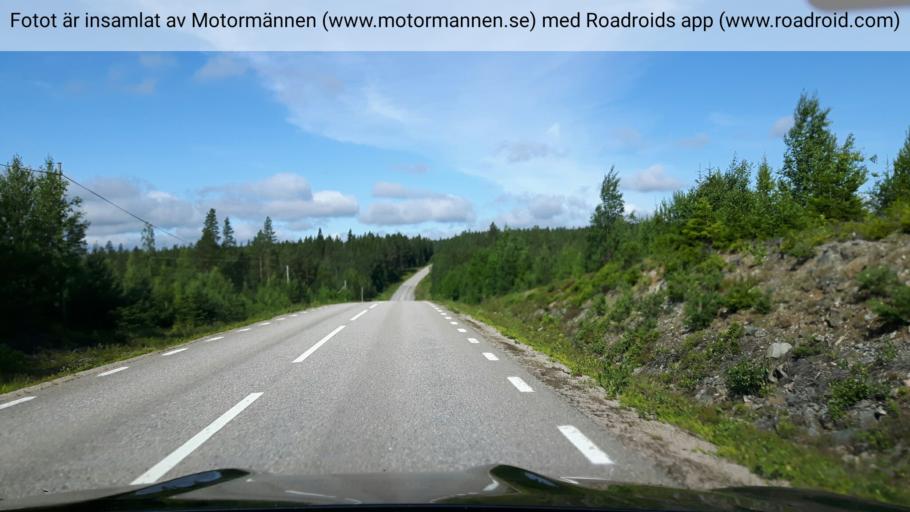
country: SE
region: Gaevleborg
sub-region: Ljusdals Kommun
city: Farila
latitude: 61.7606
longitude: 15.5118
